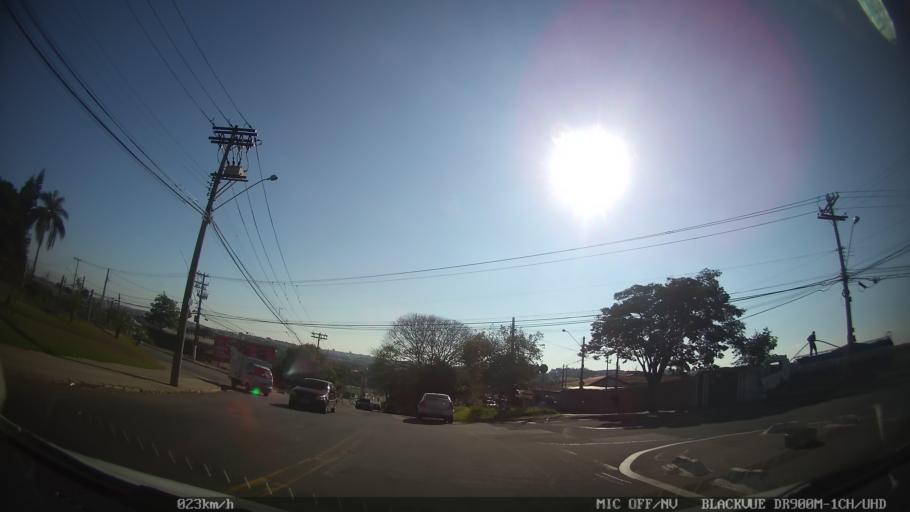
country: BR
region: Sao Paulo
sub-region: Campinas
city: Campinas
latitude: -22.9637
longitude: -47.1076
